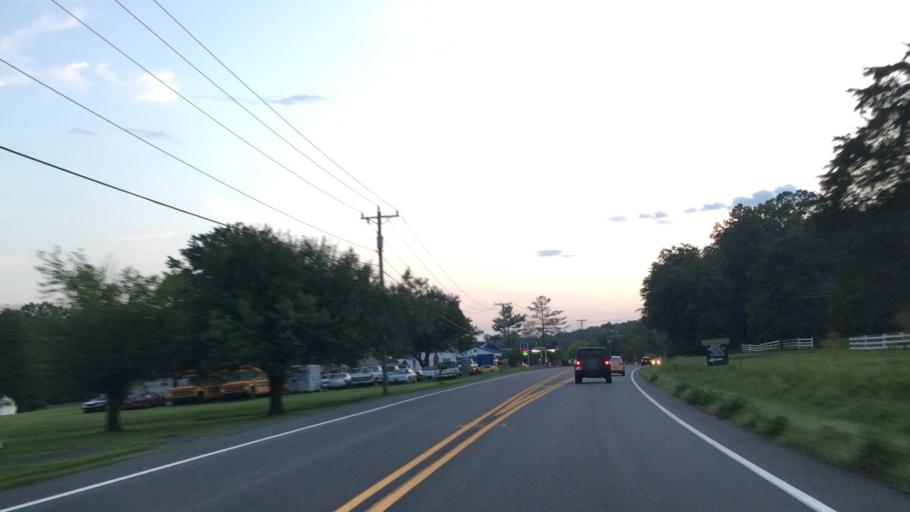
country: US
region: Virginia
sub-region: Orange County
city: Orange
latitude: 38.2428
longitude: -78.0567
